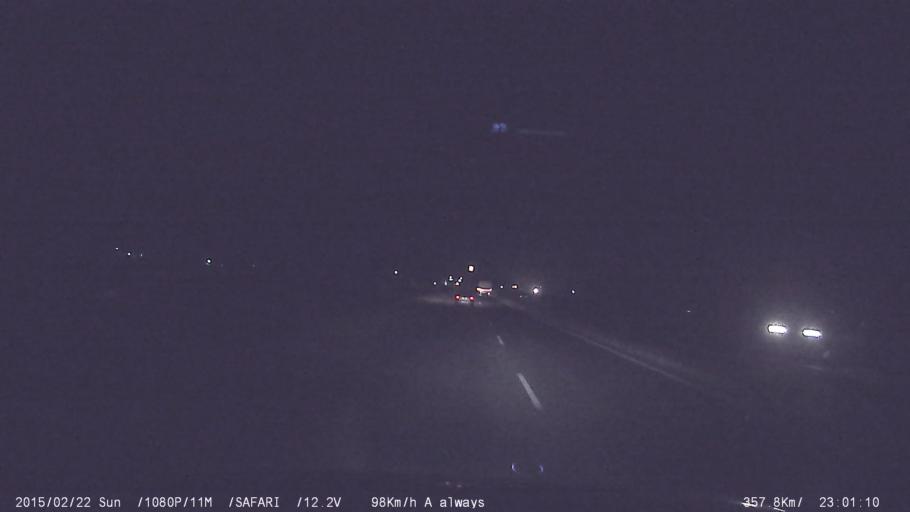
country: IN
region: Tamil Nadu
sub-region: Namakkal
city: Rasipuram
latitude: 11.3592
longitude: 78.1653
